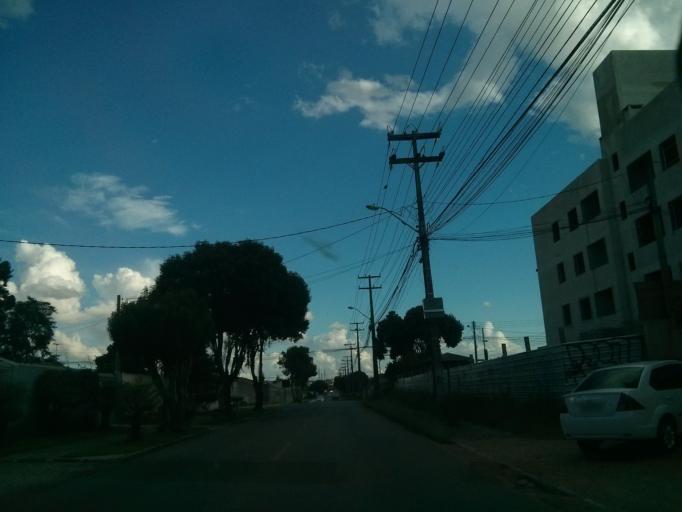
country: BR
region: Parana
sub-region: Sao Jose Dos Pinhais
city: Sao Jose dos Pinhais
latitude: -25.5194
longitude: -49.2314
